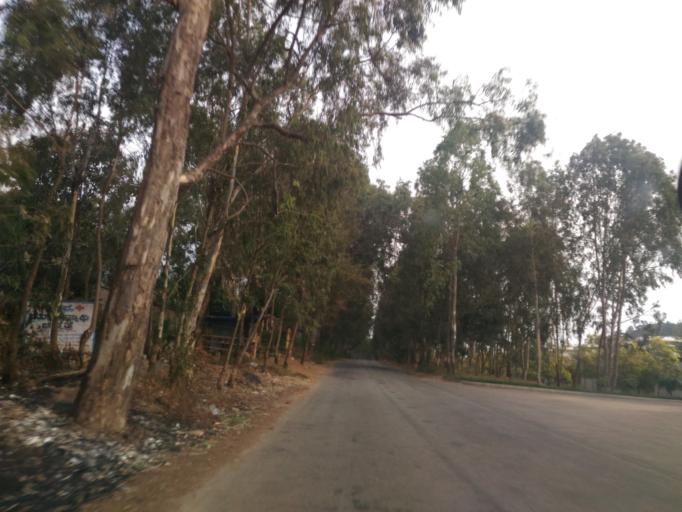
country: IN
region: Karnataka
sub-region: Chikkaballapur
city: Chik Ballapur
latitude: 13.3487
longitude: 77.6671
